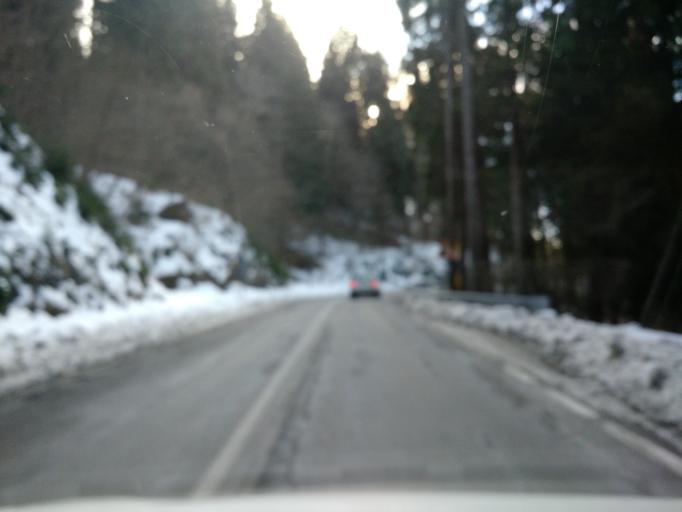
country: IT
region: Veneto
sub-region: Provincia di Vicenza
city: Canove di Roana
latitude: 45.8744
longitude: 11.4796
